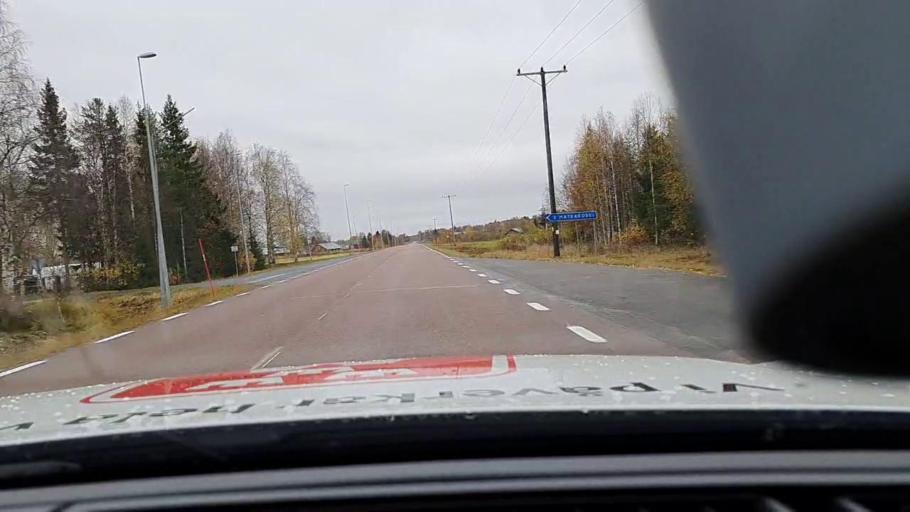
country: FI
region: Lapland
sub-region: Torniolaakso
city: Ylitornio
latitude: 66.1413
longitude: 23.8992
